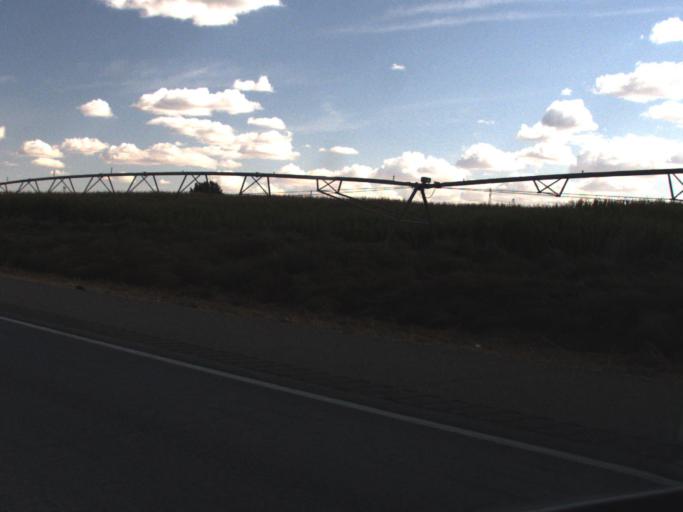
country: US
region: Washington
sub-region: Yakima County
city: Granger
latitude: 46.3383
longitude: -120.1586
